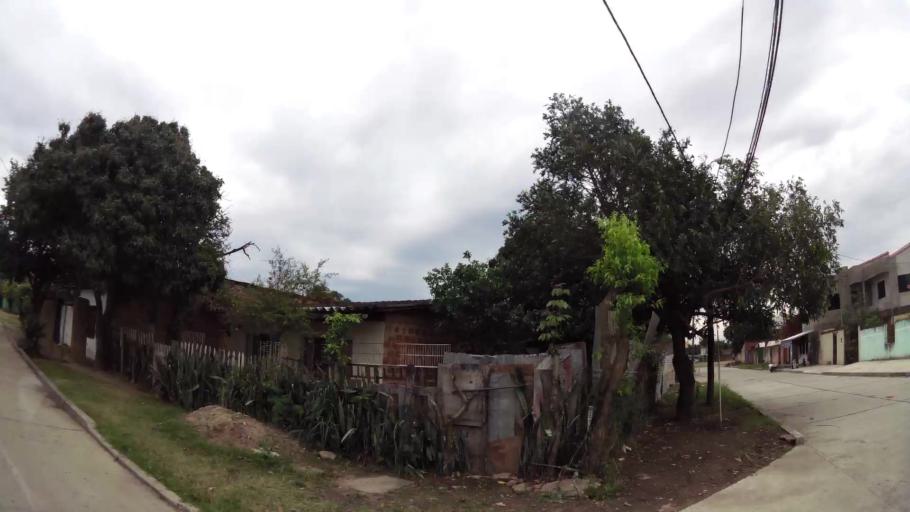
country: BO
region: Santa Cruz
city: Santa Cruz de la Sierra
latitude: -17.7481
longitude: -63.1861
